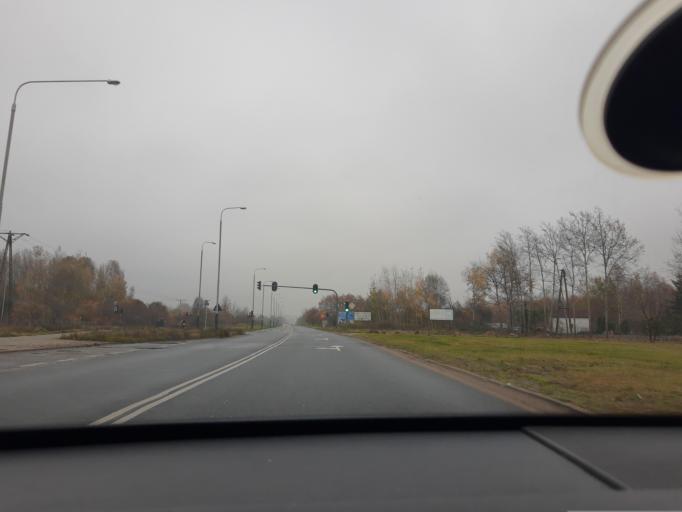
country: PL
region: Lodz Voivodeship
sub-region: Powiat pabianicki
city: Konstantynow Lodzki
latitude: 51.7322
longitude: 19.3660
